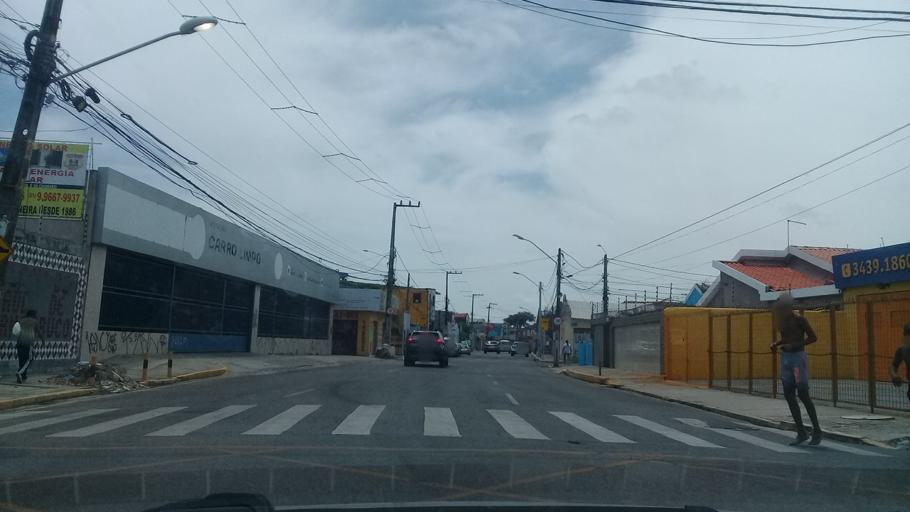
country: BR
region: Pernambuco
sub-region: Olinda
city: Olinda
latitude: -8.0113
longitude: -34.8430
